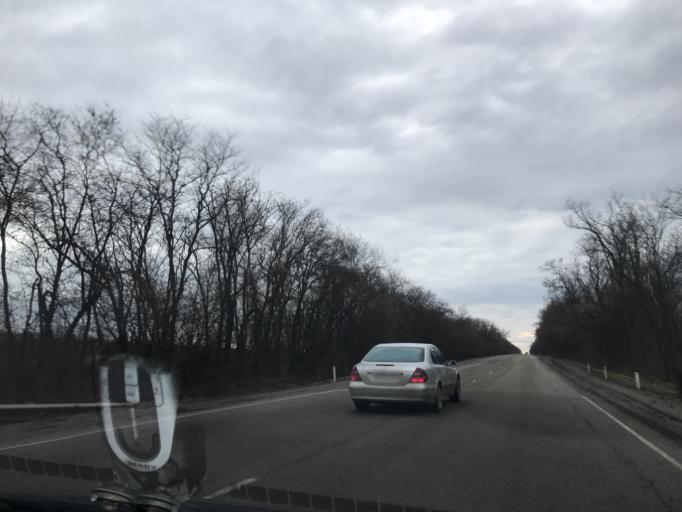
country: RU
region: Krasnodarskiy
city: Mirskoy
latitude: 45.6405
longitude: 40.3546
